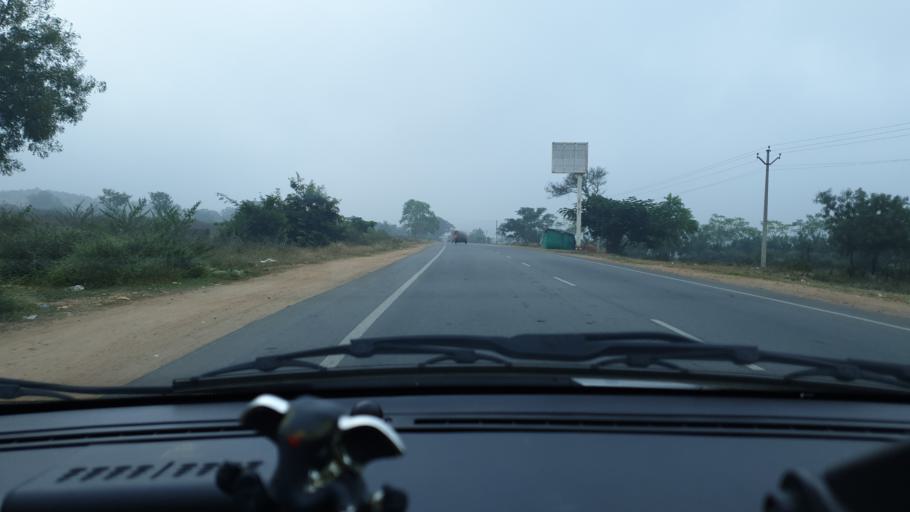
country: IN
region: Telangana
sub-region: Mahbubnagar
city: Farrukhnagar
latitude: 16.9629
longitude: 78.5112
